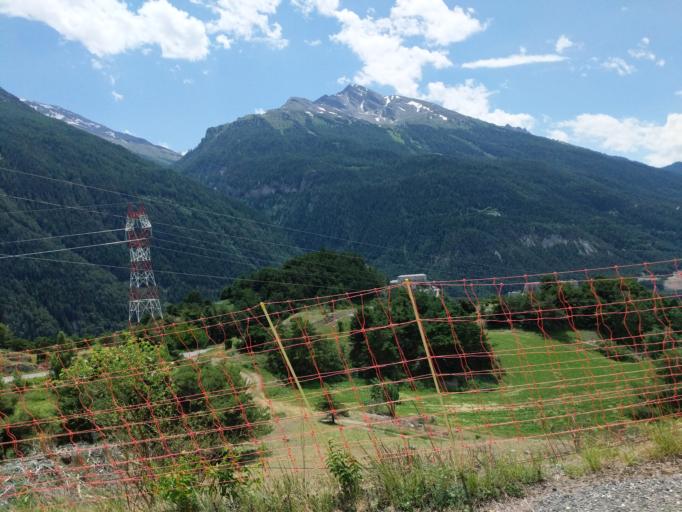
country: FR
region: Rhone-Alpes
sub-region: Departement de la Savoie
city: Modane
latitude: 45.2202
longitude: 6.7407
